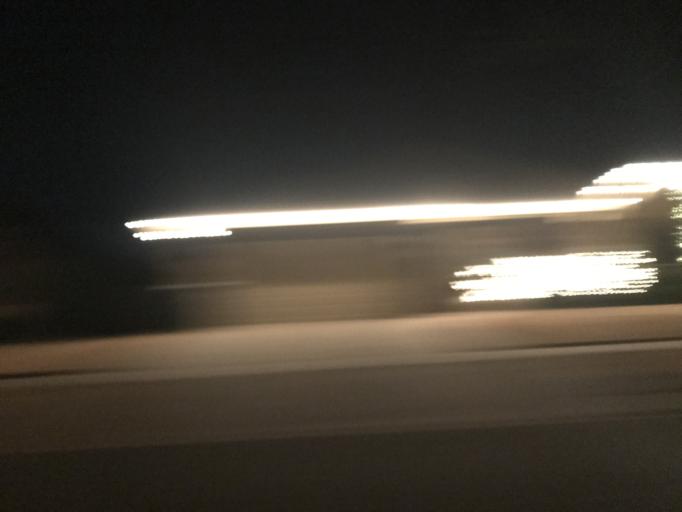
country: US
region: Texas
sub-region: Taylor County
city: Abilene
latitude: 32.3742
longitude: -99.7194
